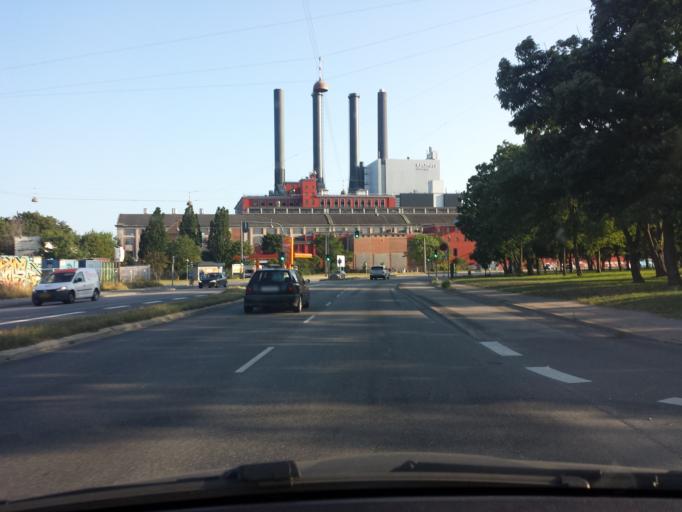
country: DK
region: Capital Region
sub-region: Kobenhavn
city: Copenhagen
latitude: 55.6595
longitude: 12.5570
